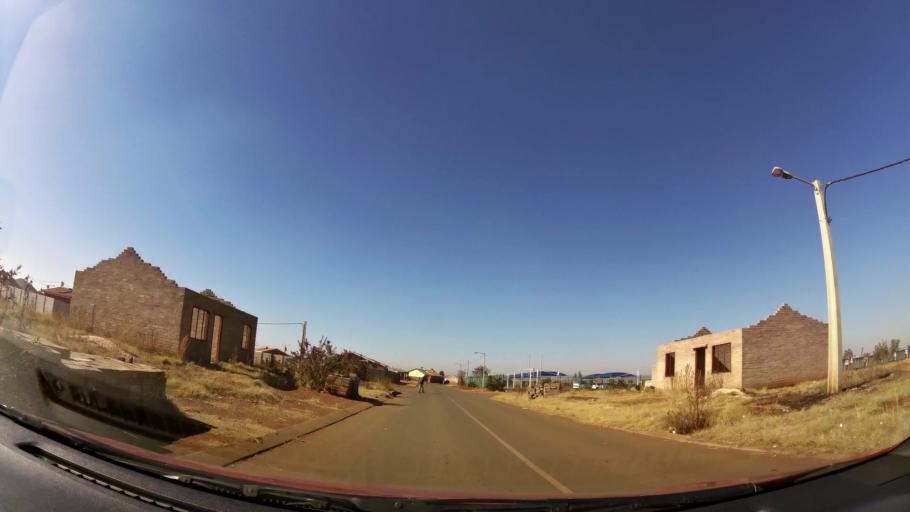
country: ZA
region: Gauteng
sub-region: City of Johannesburg Metropolitan Municipality
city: Soweto
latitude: -26.2381
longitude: 27.8010
